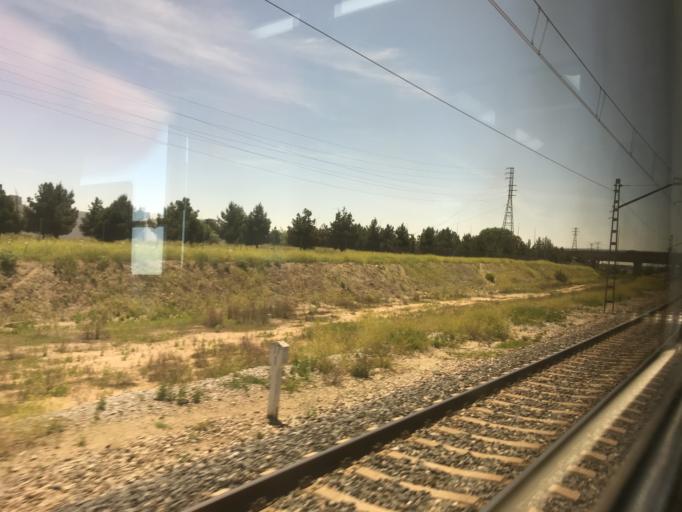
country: ES
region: Madrid
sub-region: Provincia de Madrid
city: Pinto
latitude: 40.2764
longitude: -3.7045
